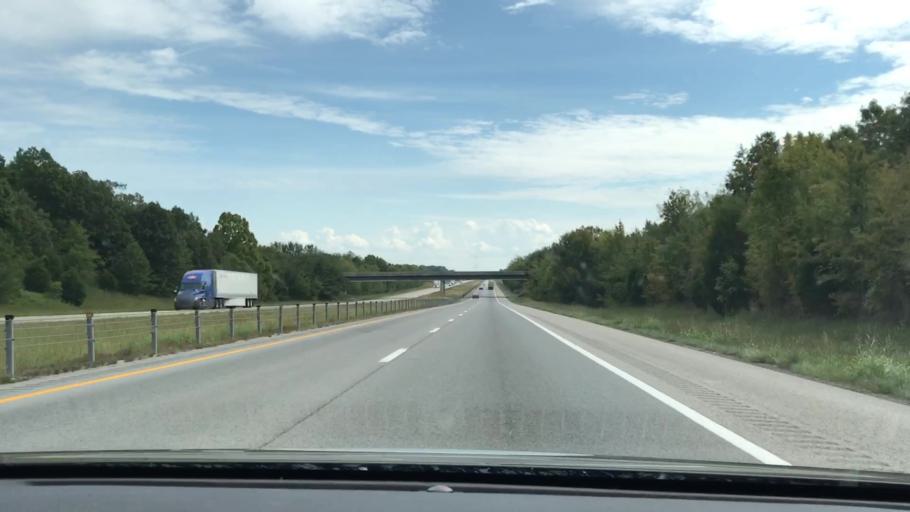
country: US
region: Kentucky
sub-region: Caldwell County
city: Princeton
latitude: 36.9917
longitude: -87.9416
